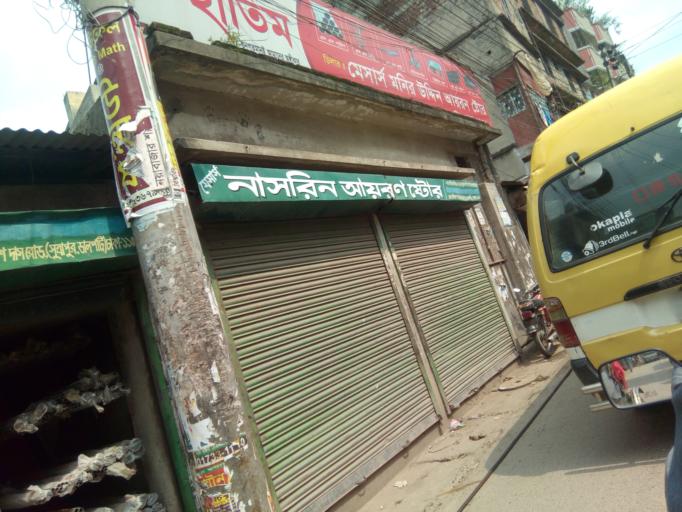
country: BD
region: Dhaka
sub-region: Dhaka
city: Dhaka
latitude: 23.7061
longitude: 90.4179
